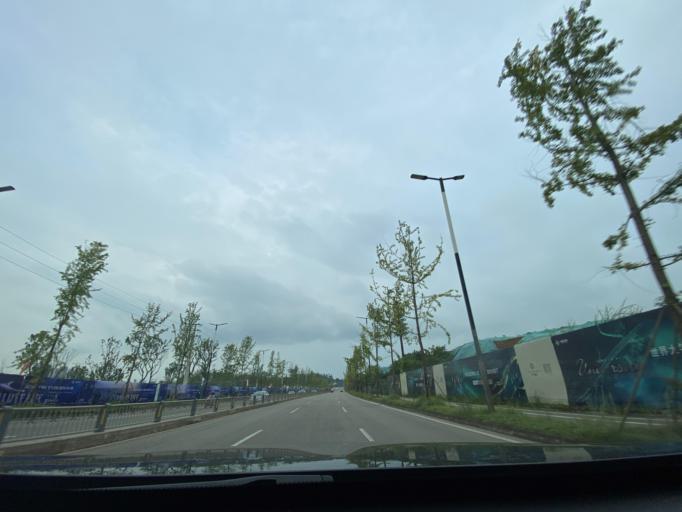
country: CN
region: Sichuan
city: Jiancheng
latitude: 30.4950
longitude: 104.4569
